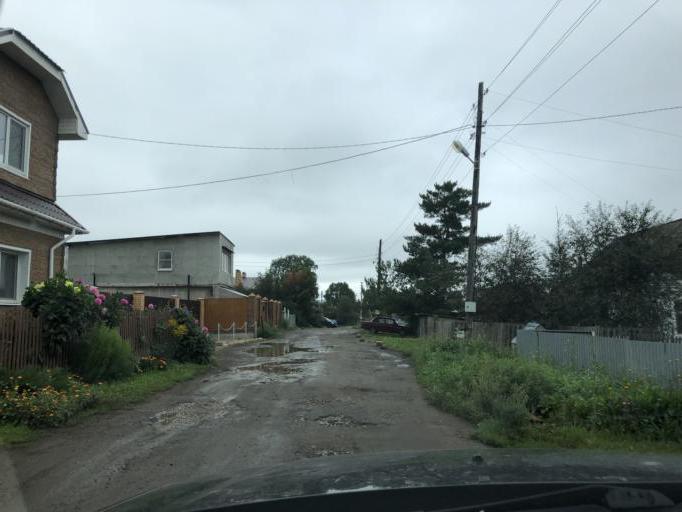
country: RU
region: Tula
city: Mendeleyevskiy
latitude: 54.1643
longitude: 37.5505
